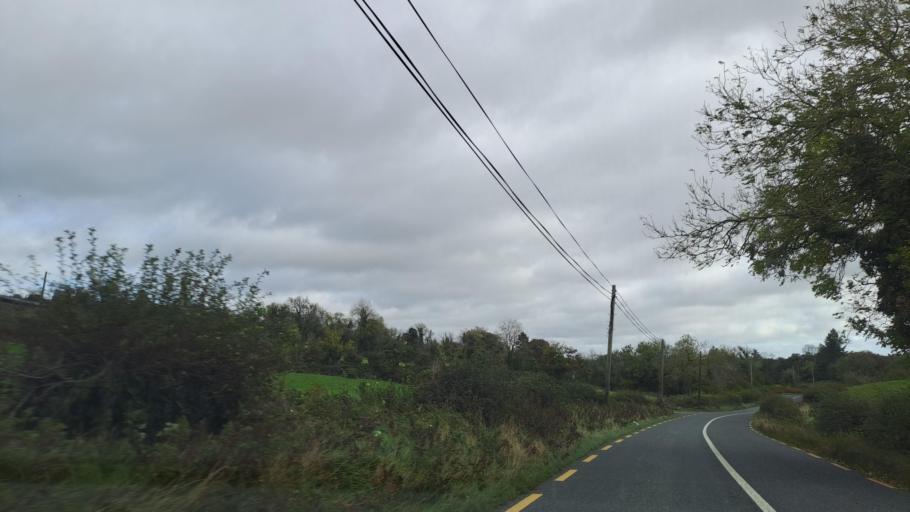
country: IE
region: Ulster
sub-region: An Cabhan
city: Kingscourt
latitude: 53.9106
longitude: -6.8372
